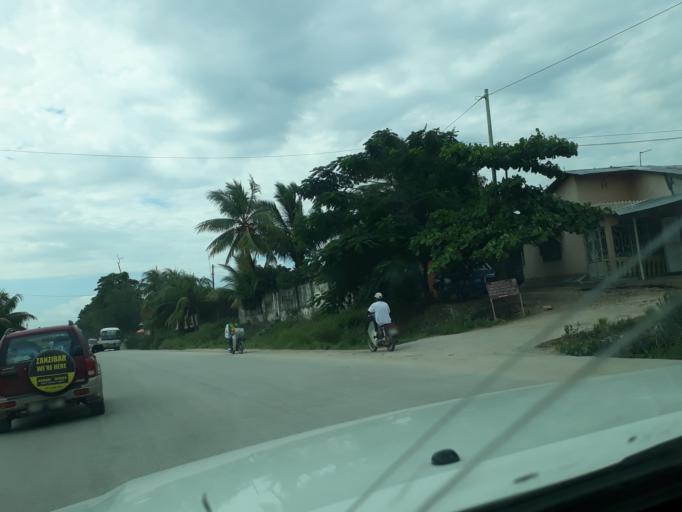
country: TZ
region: Zanzibar Central/South
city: Koani
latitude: -6.0878
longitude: 39.2226
